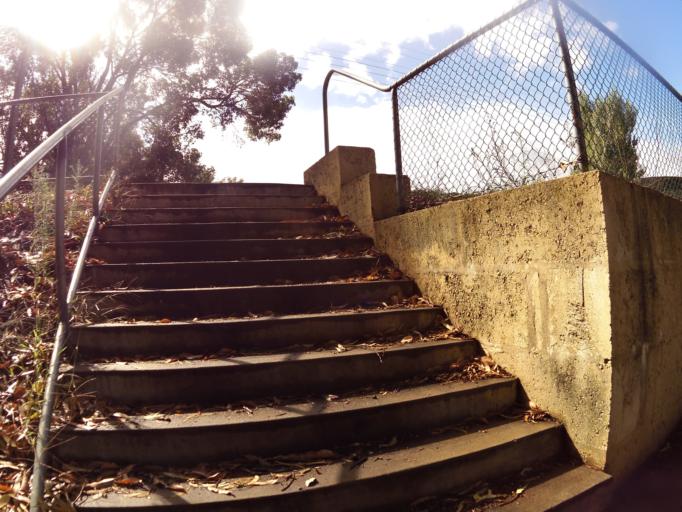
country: AU
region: Western Australia
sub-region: Donnybrook-Balingup
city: Donnybrook
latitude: -33.5714
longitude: 115.8262
